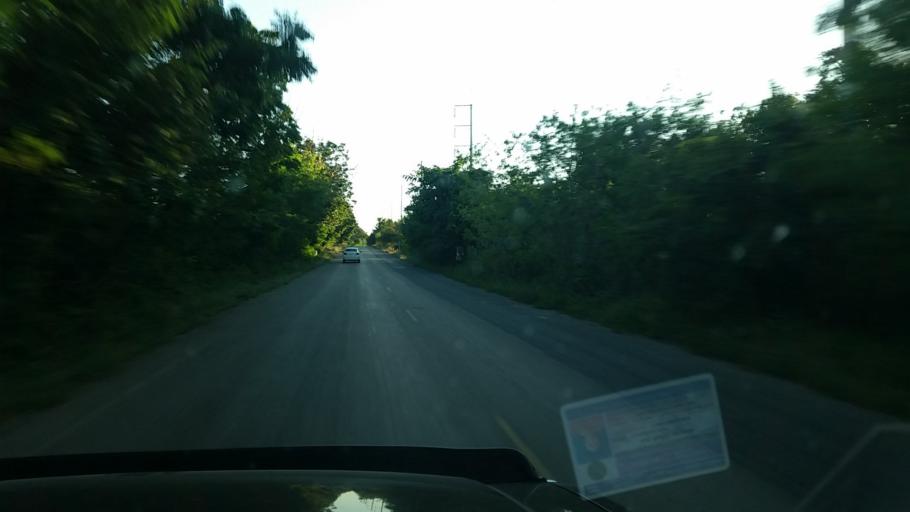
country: TH
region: Chaiyaphum
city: Sap Yai
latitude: 15.6741
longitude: 101.6753
